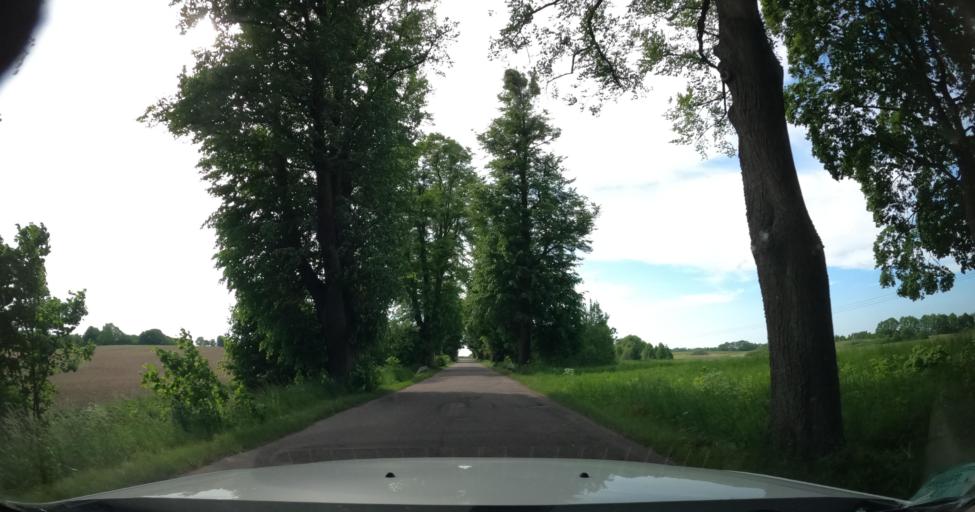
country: PL
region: Warmian-Masurian Voivodeship
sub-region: Powiat ostrodzki
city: Milakowo
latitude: 54.0170
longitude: 20.0533
